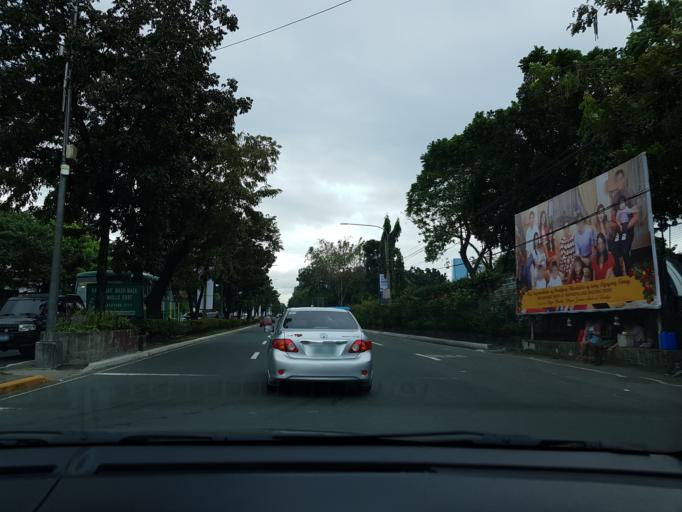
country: PH
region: Metro Manila
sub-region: San Juan
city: San Juan
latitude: 14.5997
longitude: 121.0497
